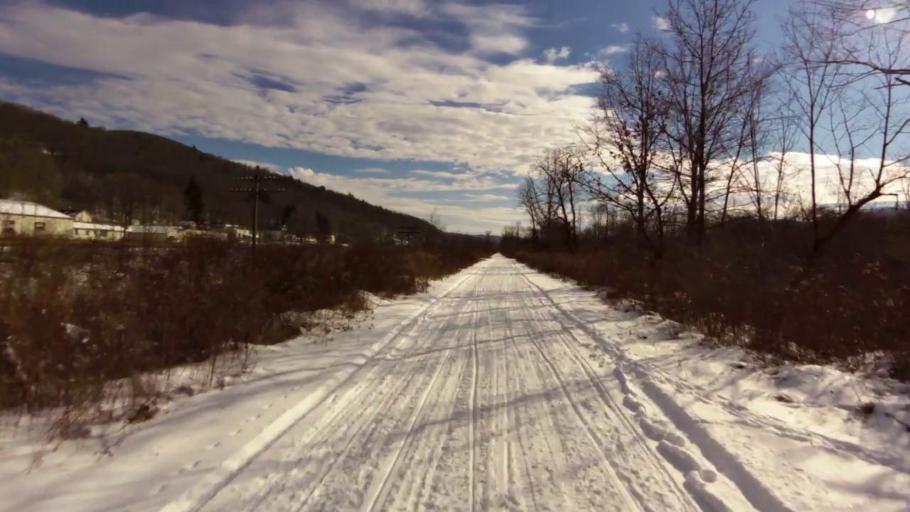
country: US
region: Pennsylvania
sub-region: McKean County
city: Foster Brook
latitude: 42.0214
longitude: -78.6295
